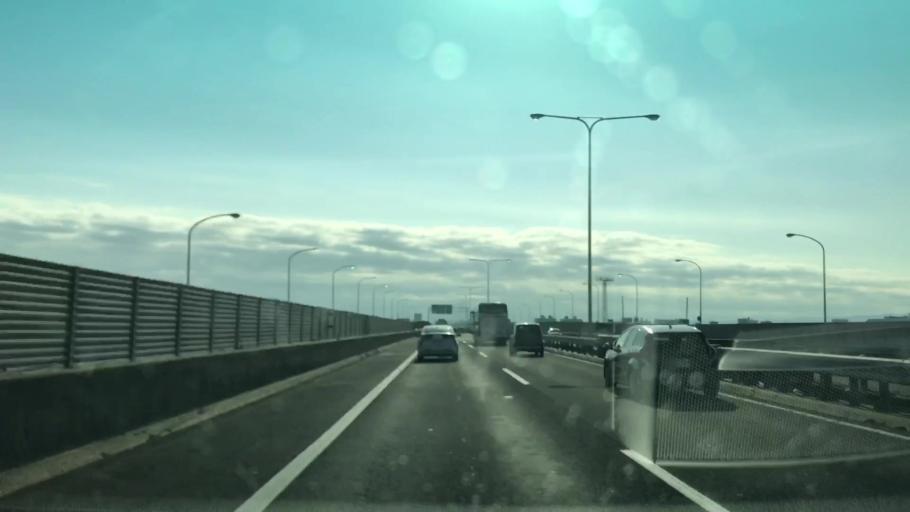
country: JP
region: Hokkaido
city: Sapporo
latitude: 43.0491
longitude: 141.4327
